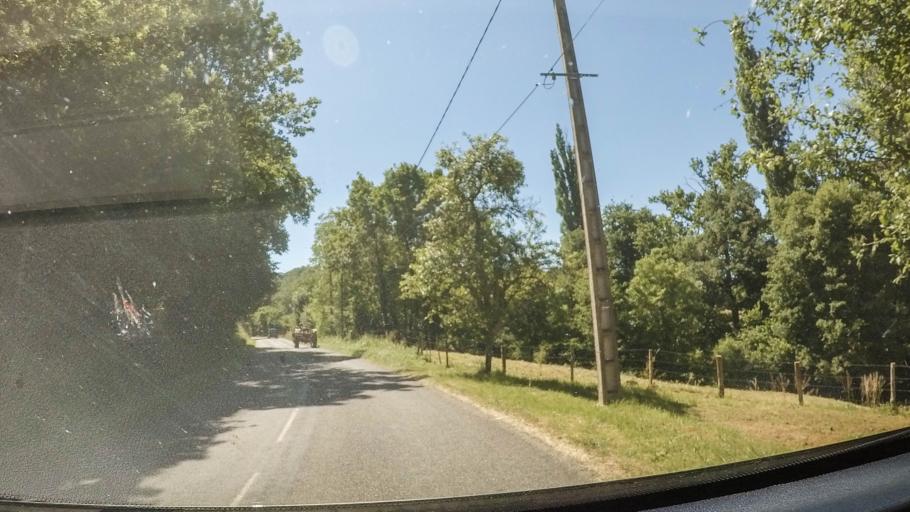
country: FR
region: Midi-Pyrenees
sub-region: Departement de l'Aveyron
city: Saint-Christophe-Vallon
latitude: 44.4658
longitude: 2.3778
